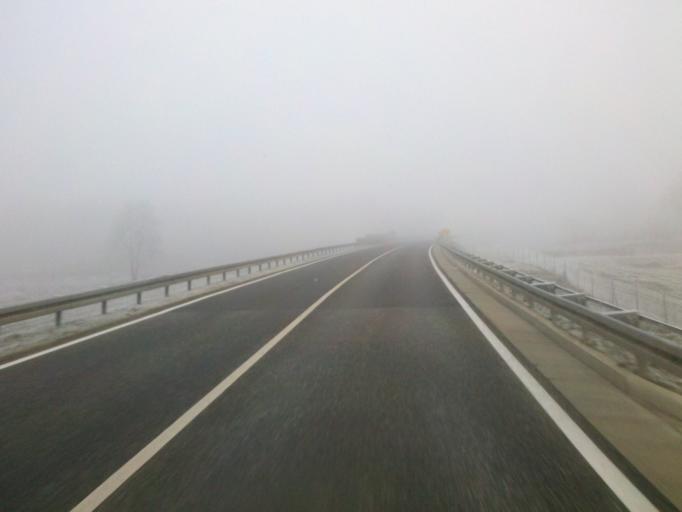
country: HR
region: Varazdinska
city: Jalkovec
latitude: 46.2730
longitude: 16.3030
